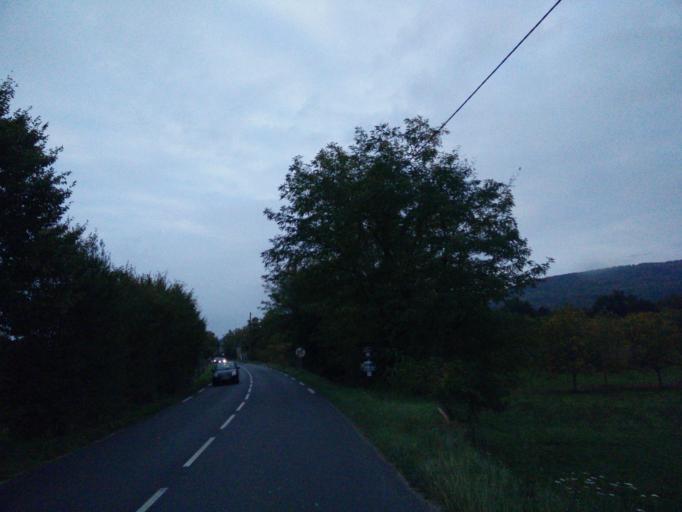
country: FR
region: Aquitaine
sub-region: Departement de la Dordogne
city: Carsac-Aillac
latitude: 44.8324
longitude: 1.2752
